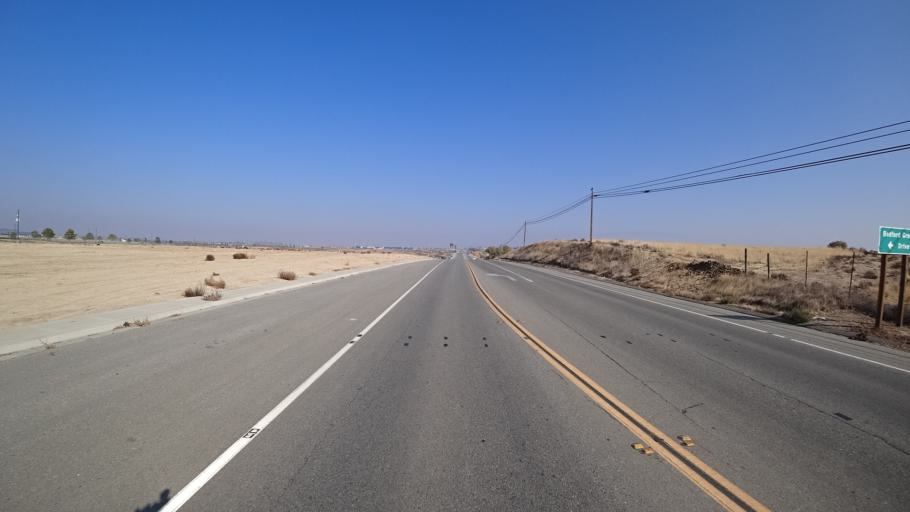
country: US
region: California
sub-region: Kern County
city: Bakersfield
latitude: 35.3888
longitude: -118.8913
